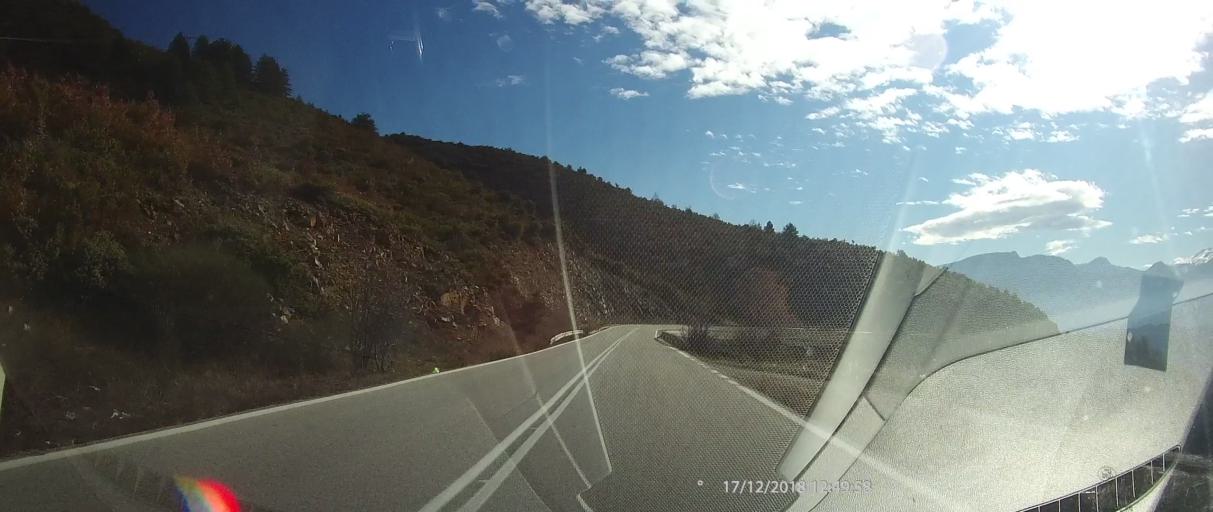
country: GR
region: Thessaly
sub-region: Trikala
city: Kastraki
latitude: 39.7753
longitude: 21.4504
